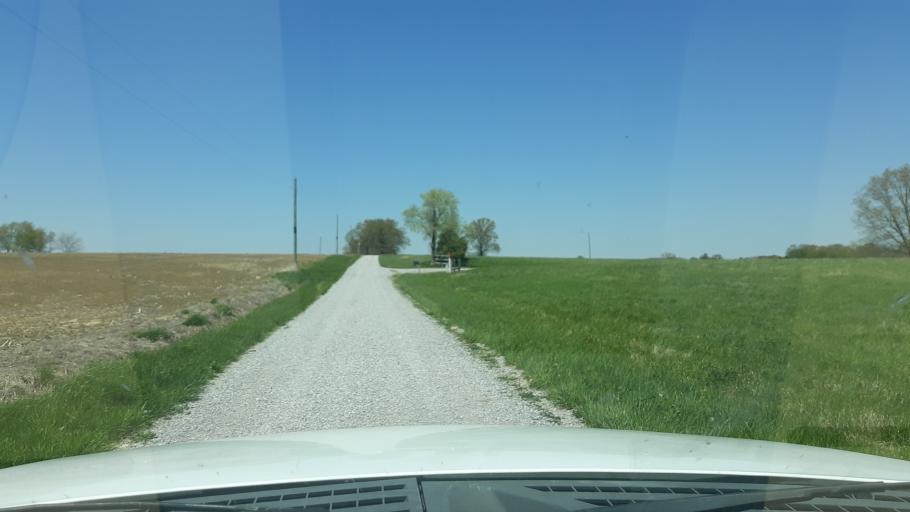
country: US
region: Illinois
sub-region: Saline County
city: Harrisburg
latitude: 37.8823
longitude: -88.6421
